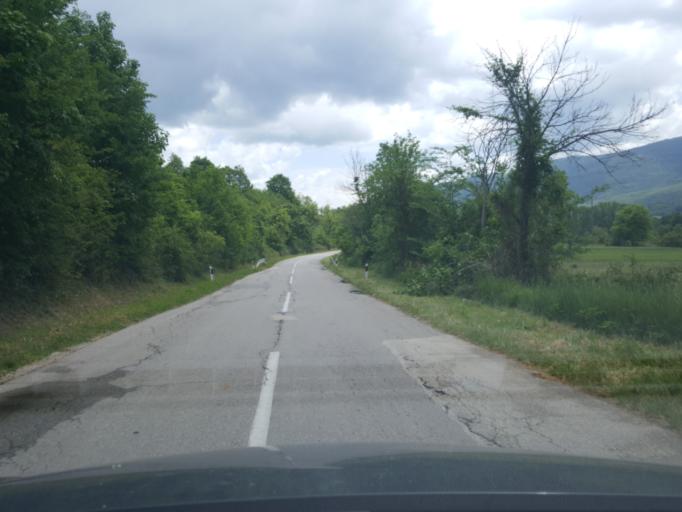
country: RS
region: Central Serbia
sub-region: Zajecarski Okrug
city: Soko Banja
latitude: 43.6466
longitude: 21.9308
